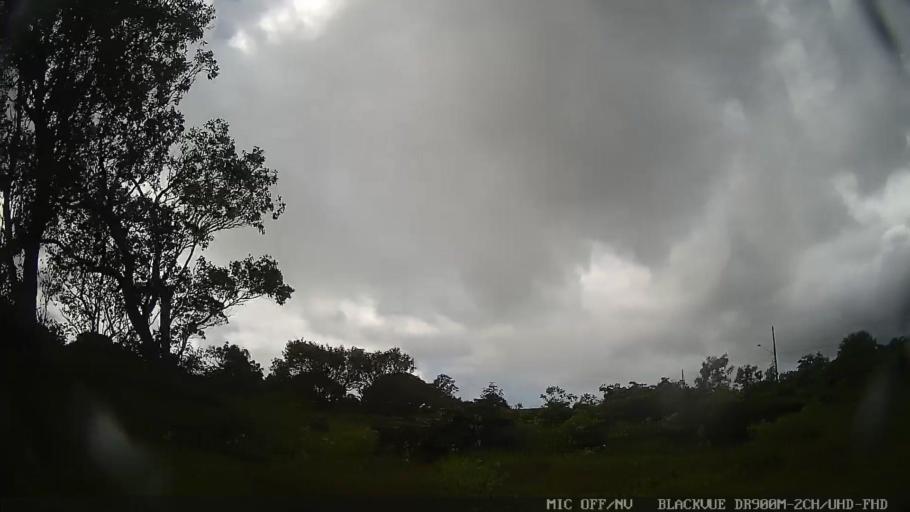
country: BR
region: Sao Paulo
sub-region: Peruibe
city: Peruibe
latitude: -24.2476
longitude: -46.8972
